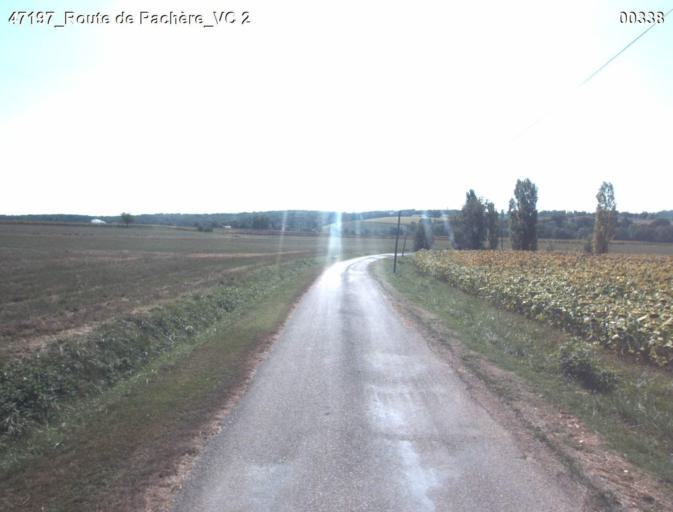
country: FR
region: Aquitaine
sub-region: Departement du Lot-et-Garonne
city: Laplume
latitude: 44.0894
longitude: 0.4674
